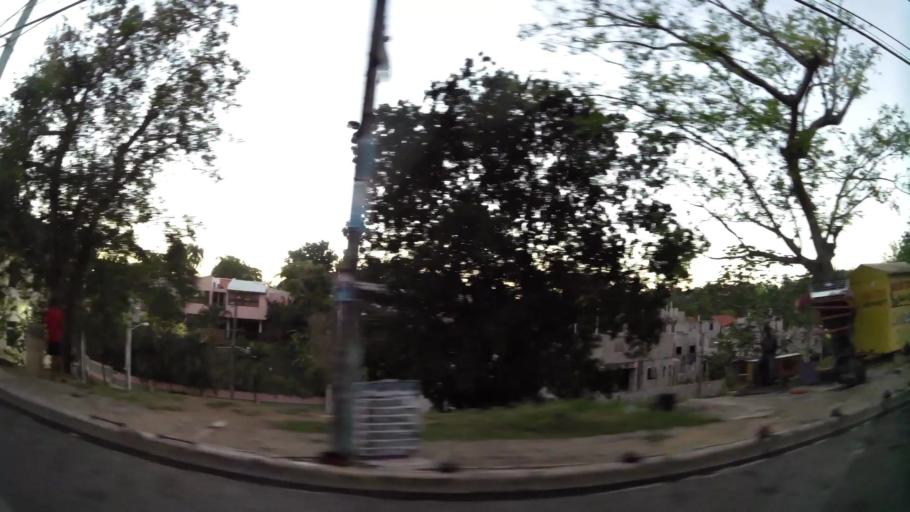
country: DO
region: Nacional
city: La Agustina
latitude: 18.5058
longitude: -69.9502
